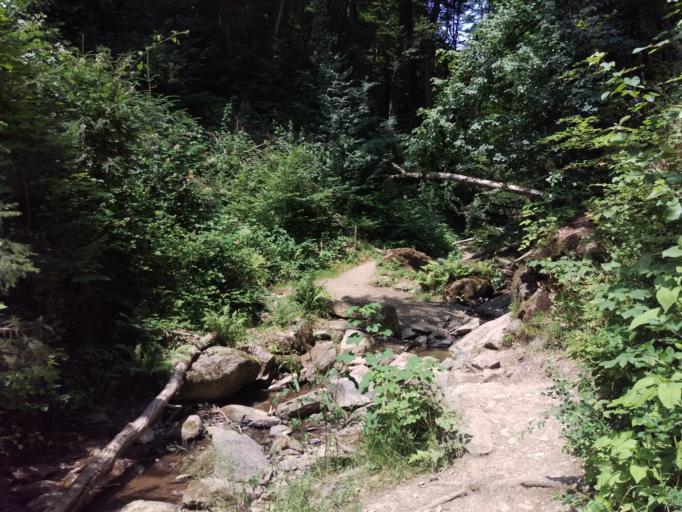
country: AT
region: Styria
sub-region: Graz Stadt
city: Mariatrost
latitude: 47.1076
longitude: 15.4775
